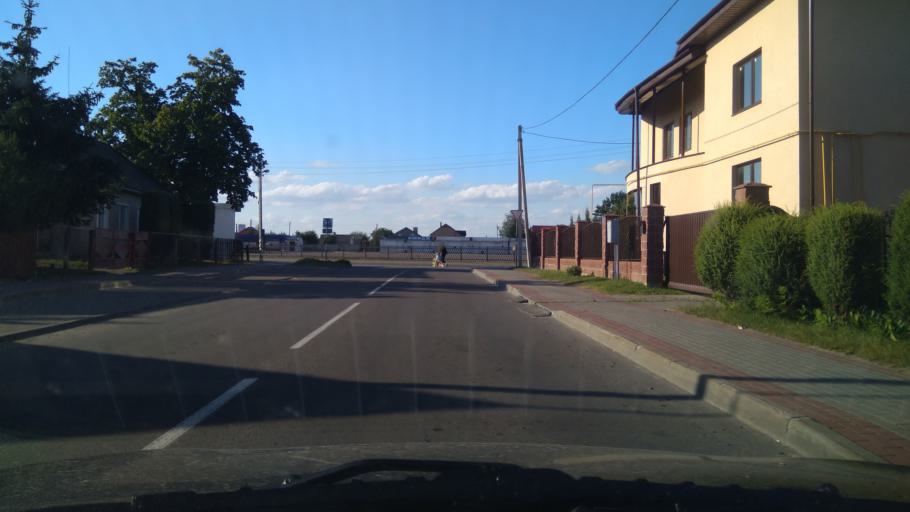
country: BY
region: Brest
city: Byaroza
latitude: 52.5400
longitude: 24.9780
